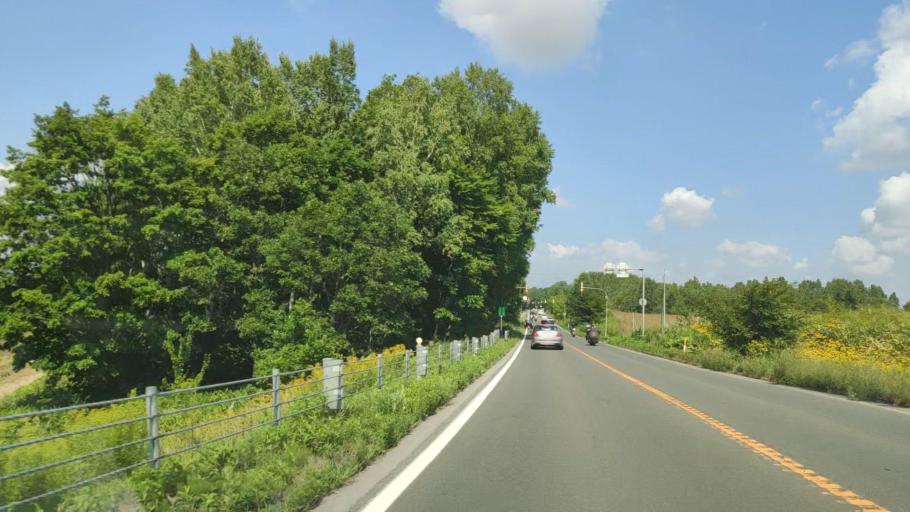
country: JP
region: Hokkaido
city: Shimo-furano
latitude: 43.5067
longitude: 142.4578
